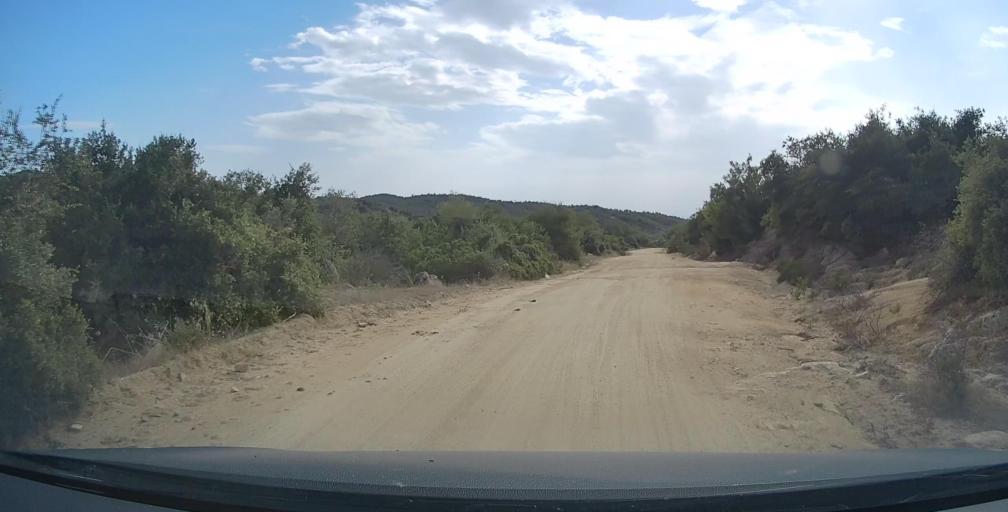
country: GR
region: Central Macedonia
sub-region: Nomos Chalkidikis
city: Sykia
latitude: 40.0087
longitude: 23.9256
